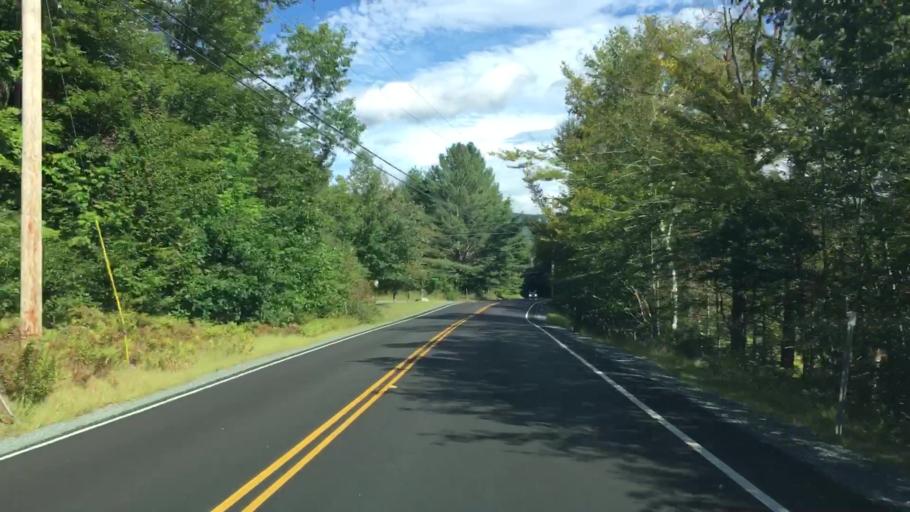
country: US
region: New Hampshire
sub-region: Grafton County
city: Woodstock
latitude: 44.0294
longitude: -71.7098
